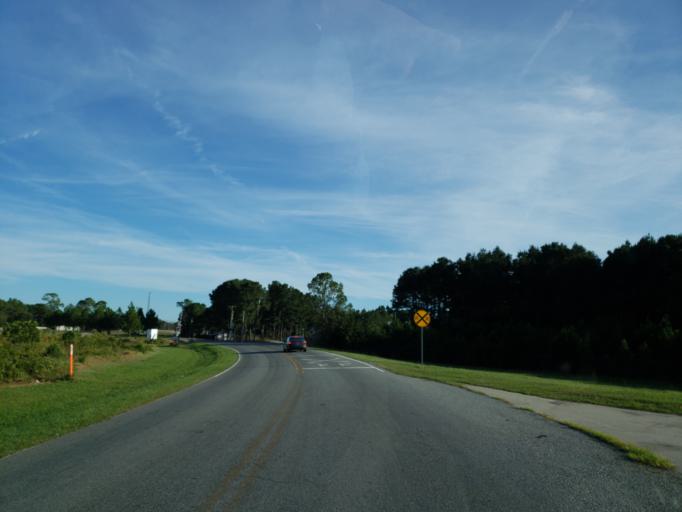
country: US
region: Georgia
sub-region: Dooly County
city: Vienna
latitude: 32.0780
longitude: -83.7879
